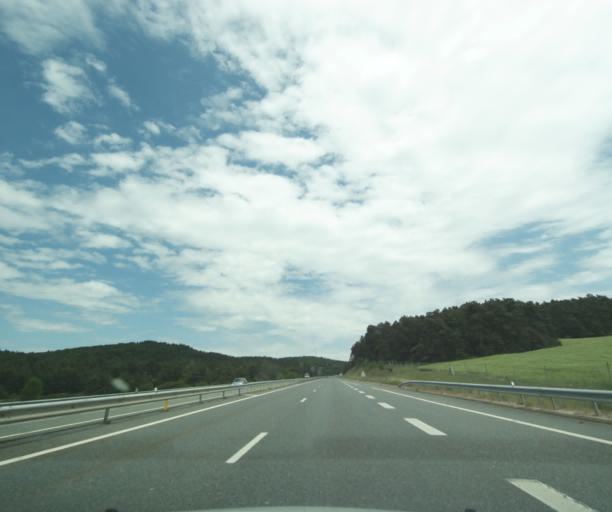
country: FR
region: Midi-Pyrenees
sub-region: Departement de l'Aveyron
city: Severac-le-Chateau
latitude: 44.3872
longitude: 3.1202
